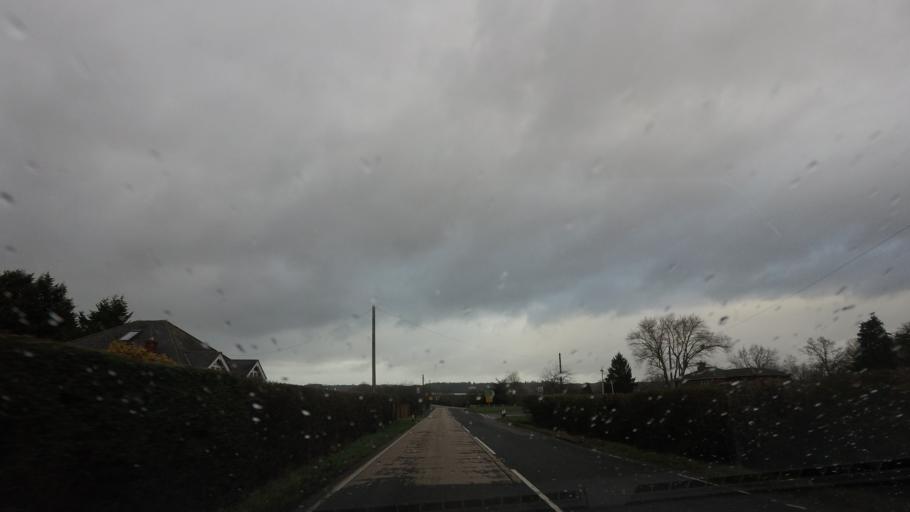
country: GB
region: England
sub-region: Kent
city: Marden
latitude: 51.1996
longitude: 0.5175
